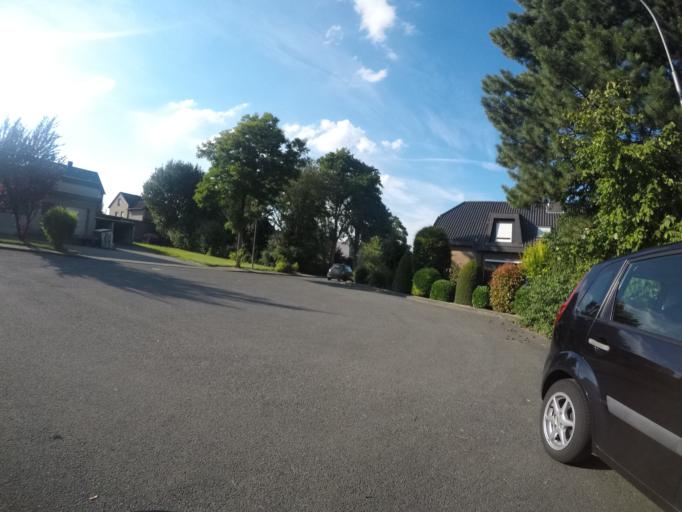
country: DE
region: North Rhine-Westphalia
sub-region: Regierungsbezirk Detmold
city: Hiddenhausen
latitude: 52.1284
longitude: 8.6313
